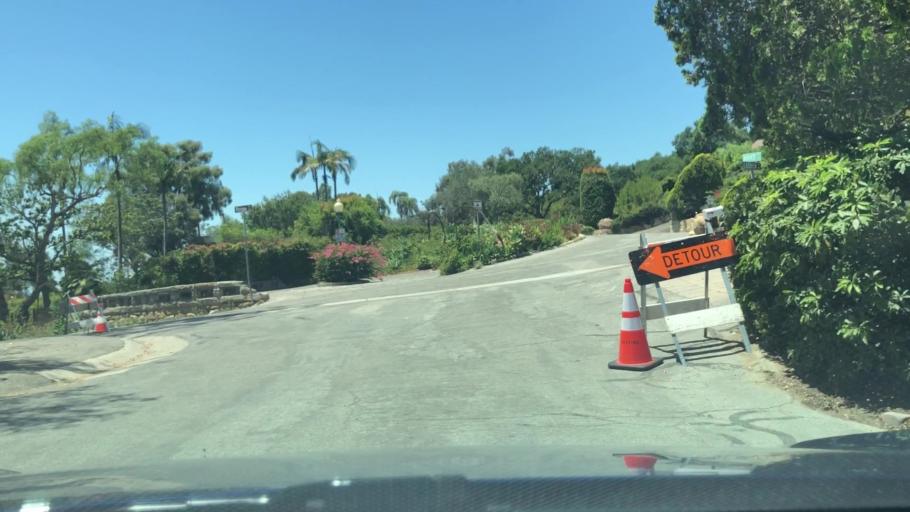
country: US
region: California
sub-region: Santa Barbara County
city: Santa Barbara
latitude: 34.4387
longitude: -119.6968
